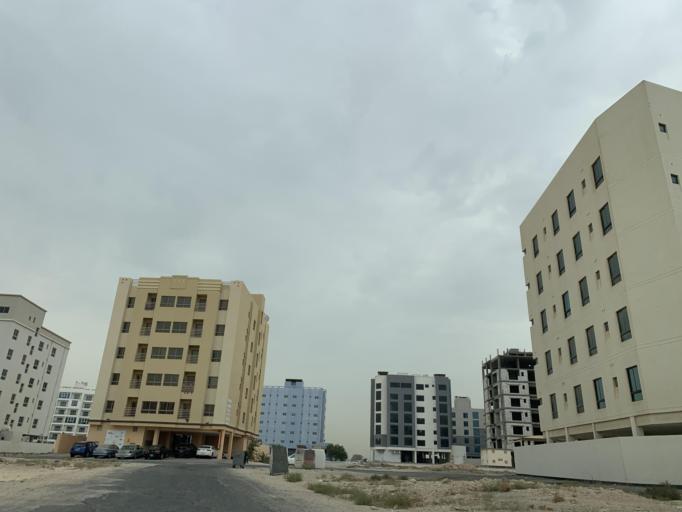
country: BH
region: Northern
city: Madinat `Isa
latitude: 26.1852
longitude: 50.4794
